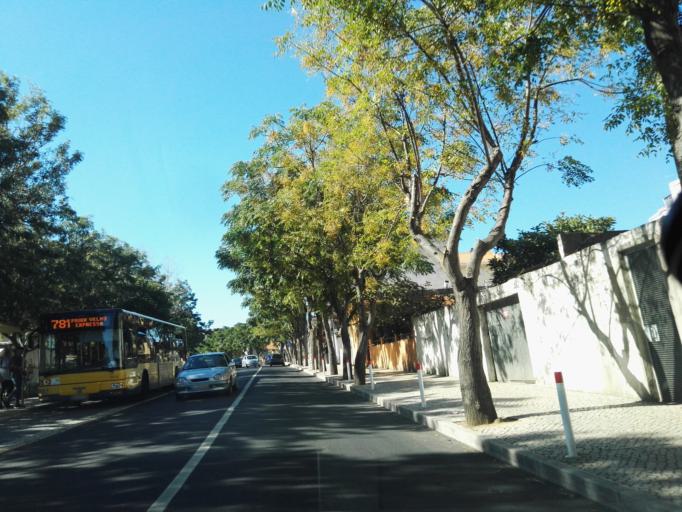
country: PT
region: Lisbon
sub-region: Loures
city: Camarate
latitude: 38.7902
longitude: -9.1237
